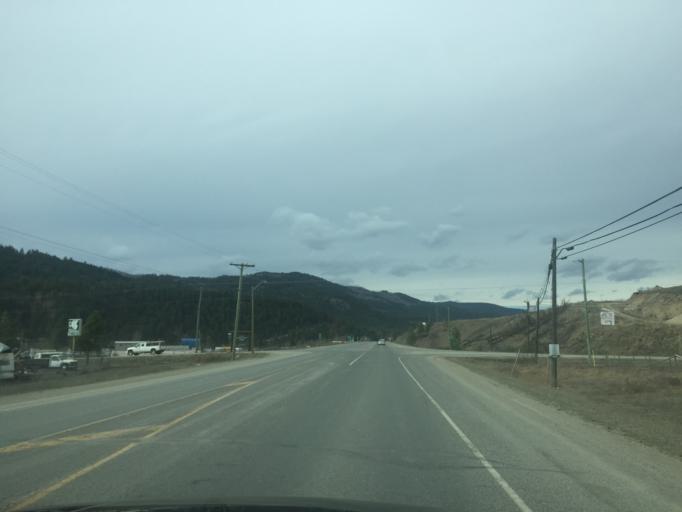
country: CA
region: British Columbia
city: Kamloops
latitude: 51.1849
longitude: -120.1421
